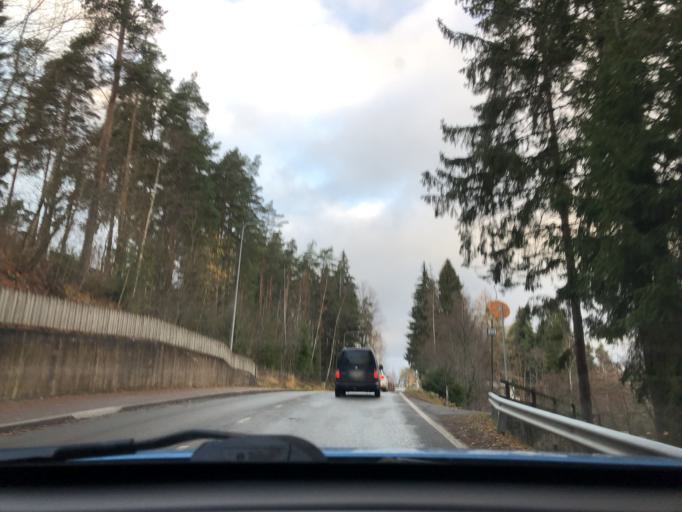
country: FI
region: Pirkanmaa
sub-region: Tampere
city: Kangasala
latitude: 61.4657
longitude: 24.0682
